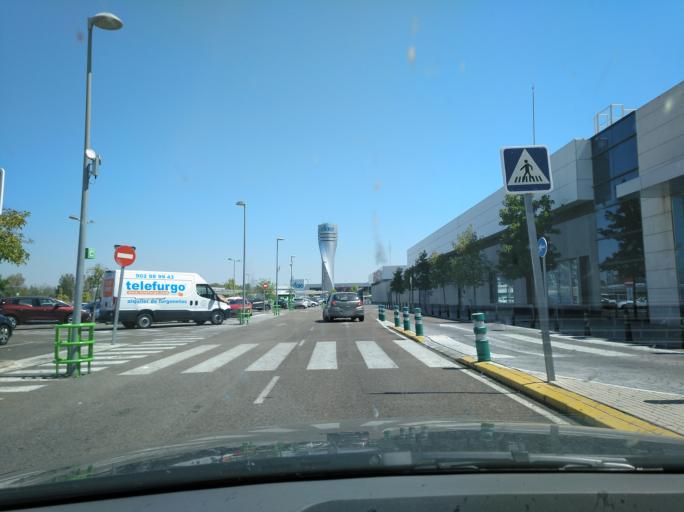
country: ES
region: Extremadura
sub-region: Provincia de Badajoz
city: Badajoz
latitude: 38.8847
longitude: -7.0240
